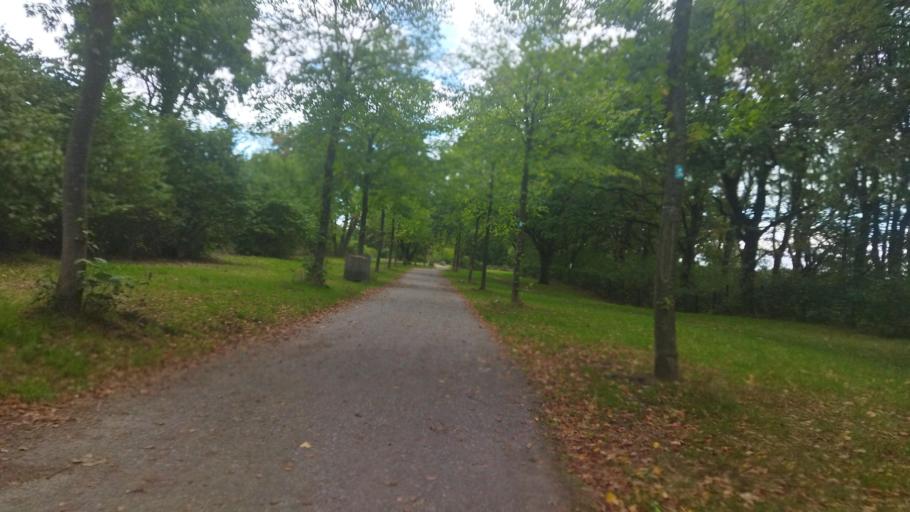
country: DE
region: North Rhine-Westphalia
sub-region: Regierungsbezirk Munster
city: Haltern
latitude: 51.7467
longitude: 7.2018
